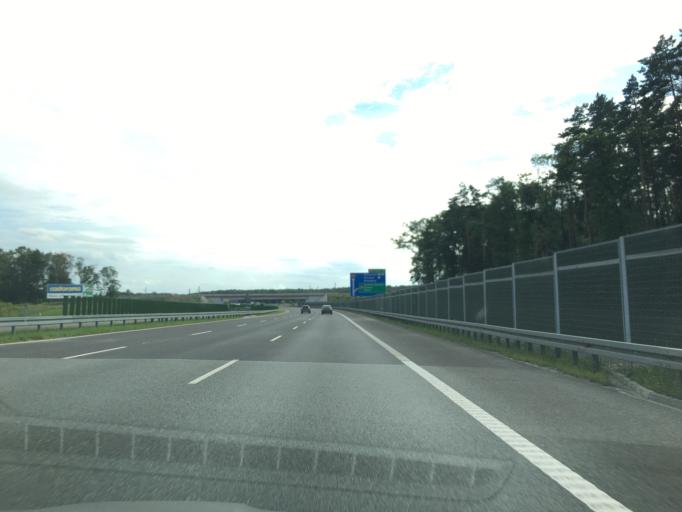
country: PL
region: Silesian Voivodeship
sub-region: Gliwice
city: Gliwice
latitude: 50.3199
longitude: 18.7265
